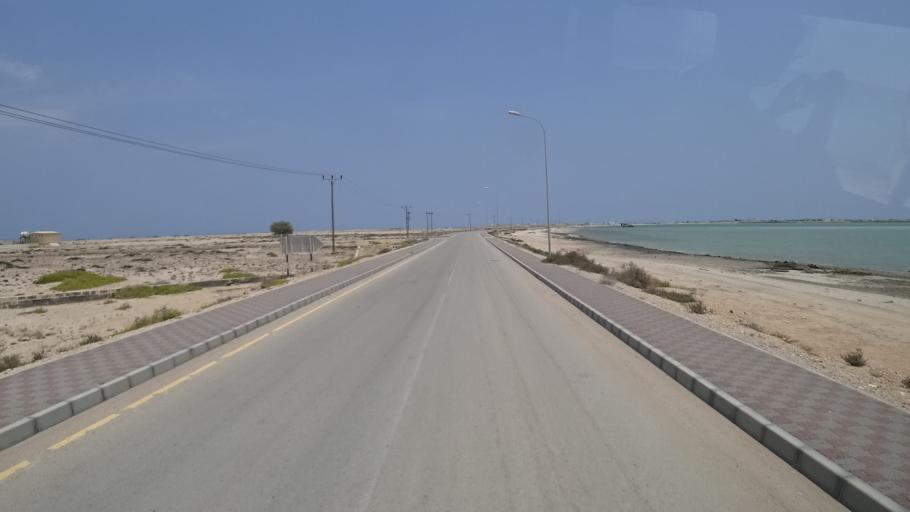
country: OM
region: Ash Sharqiyah
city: Sur
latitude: 22.5279
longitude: 59.7654
